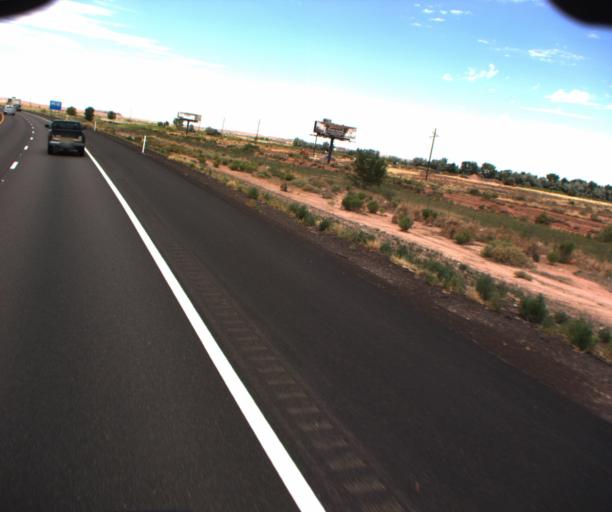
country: US
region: Arizona
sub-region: Navajo County
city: Winslow
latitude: 35.0353
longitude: -110.6873
